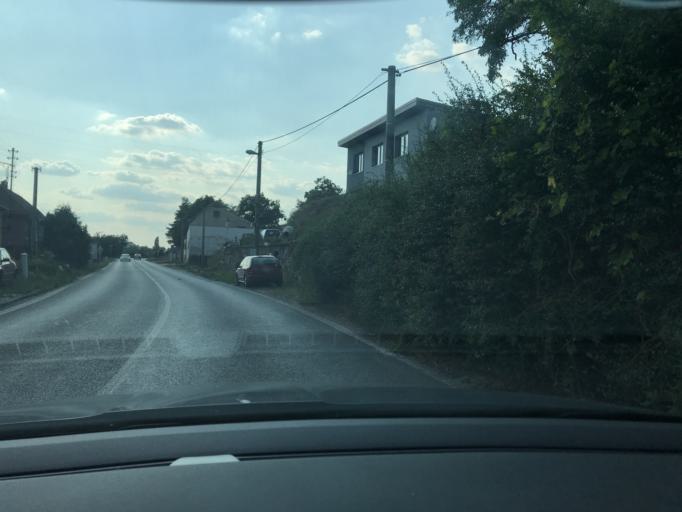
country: CZ
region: Central Bohemia
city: Kralupy nad Vltavou
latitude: 50.2327
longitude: 14.2791
